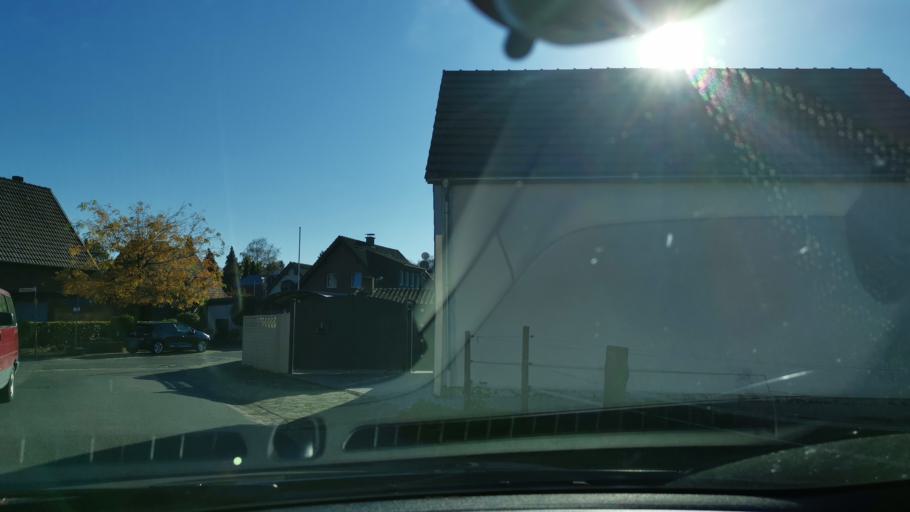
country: DE
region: North Rhine-Westphalia
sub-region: Regierungsbezirk Dusseldorf
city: Rommerskirchen
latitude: 51.0480
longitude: 6.7091
